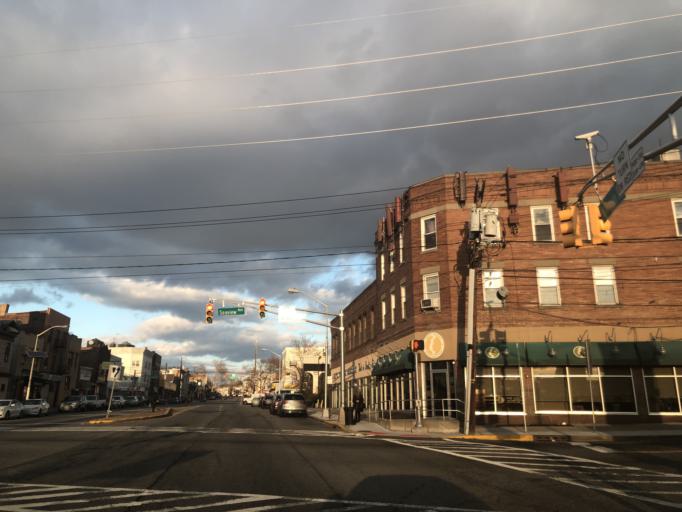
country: US
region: New Jersey
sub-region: Hudson County
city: Bayonne
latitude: 40.6953
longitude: -74.0992
